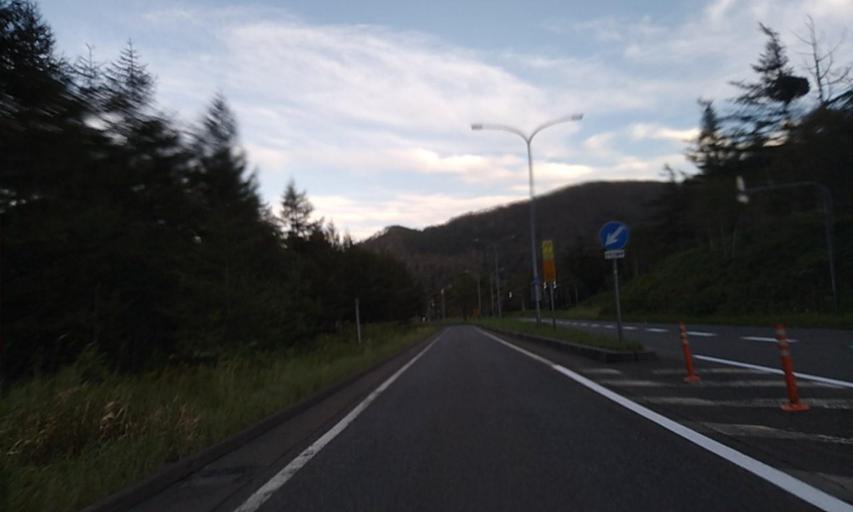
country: JP
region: Hokkaido
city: Otofuke
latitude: 42.9575
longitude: 142.7915
